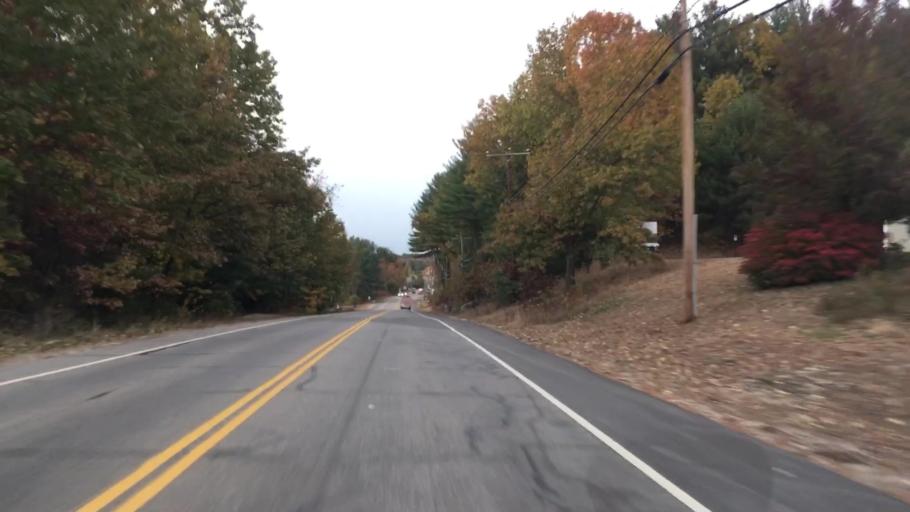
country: US
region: New Hampshire
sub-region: Hillsborough County
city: Milford
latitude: 42.8229
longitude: -71.6466
